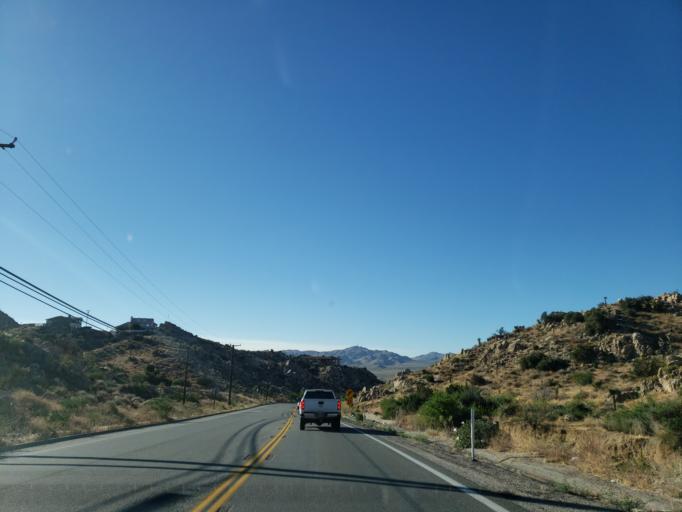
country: US
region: California
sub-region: San Bernardino County
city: Yucca Valley
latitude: 34.1451
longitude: -116.4165
